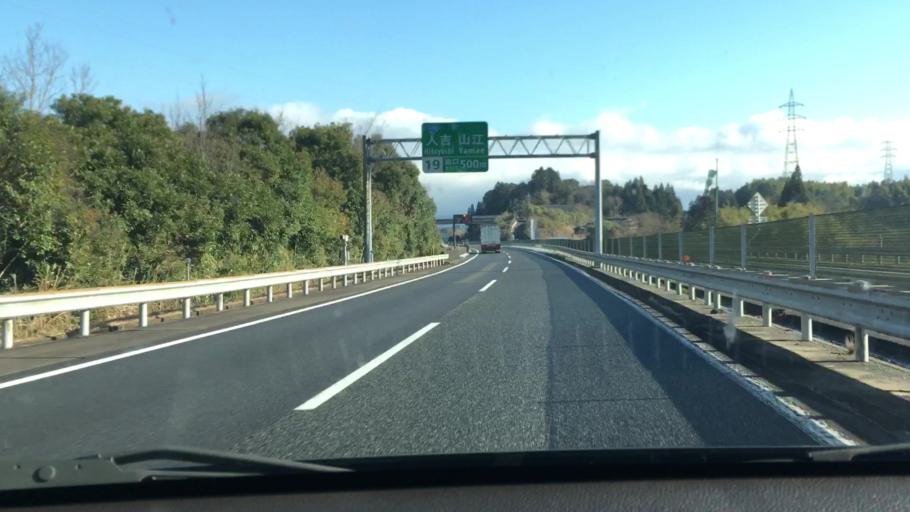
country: JP
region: Kumamoto
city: Hitoyoshi
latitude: 32.2358
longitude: 130.7642
